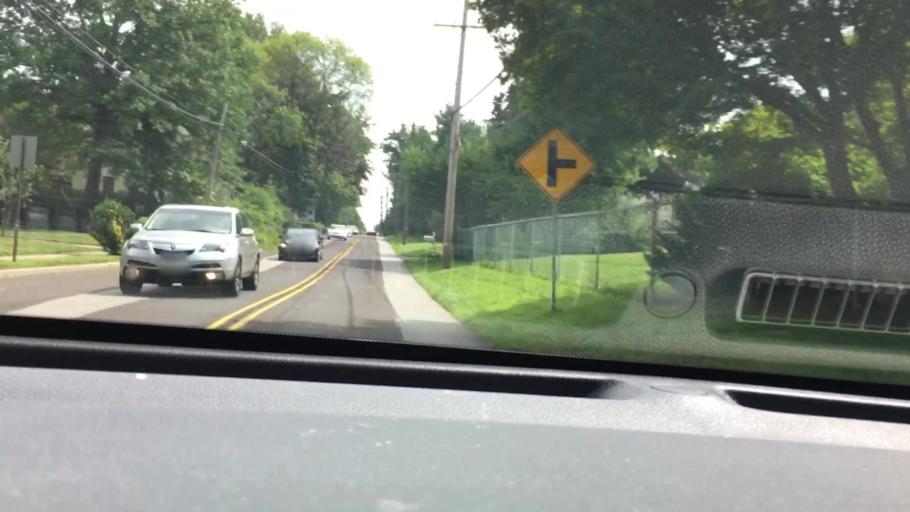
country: US
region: Pennsylvania
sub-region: Montgomery County
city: Bryn Athyn
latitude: 40.1364
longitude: -75.0368
